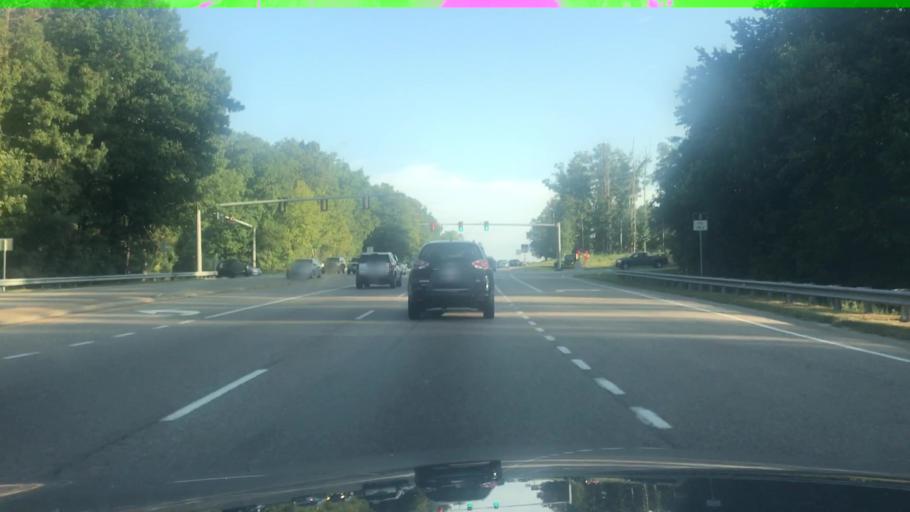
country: US
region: Virginia
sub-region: Chesterfield County
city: Brandermill
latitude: 37.4491
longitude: -77.5844
